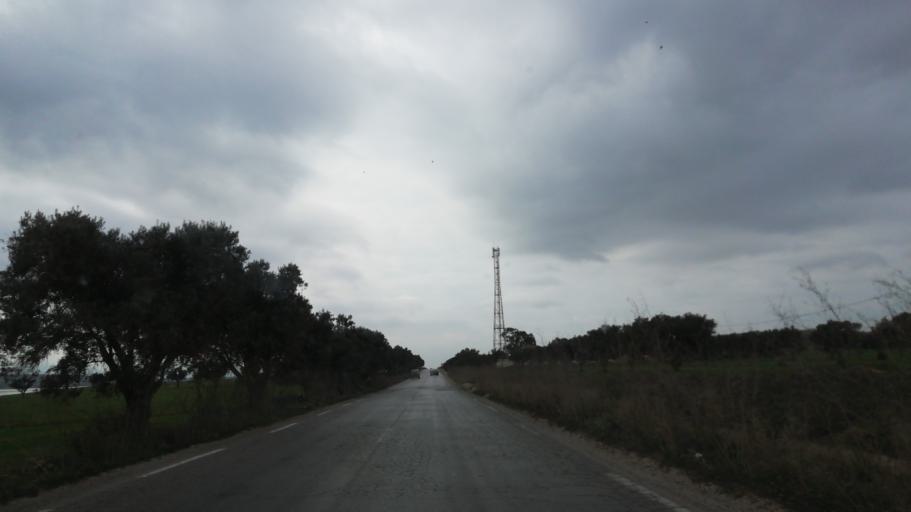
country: DZ
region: Oran
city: Sidi ech Chahmi
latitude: 35.6127
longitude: -0.4237
